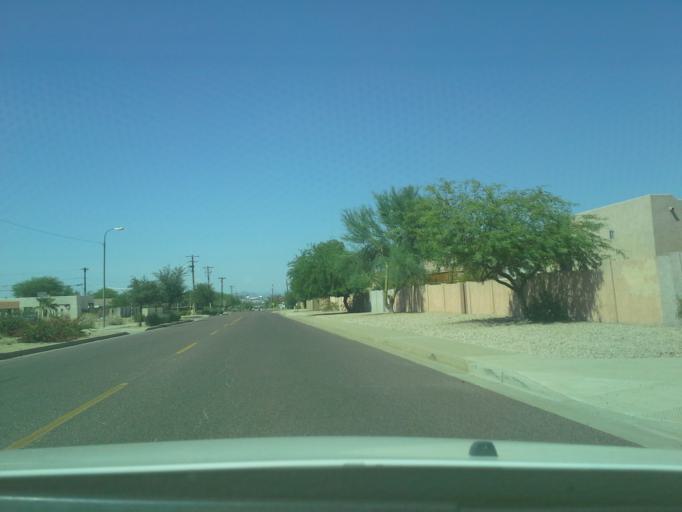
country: US
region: Arizona
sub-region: Maricopa County
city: Phoenix
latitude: 33.3617
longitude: -112.0660
